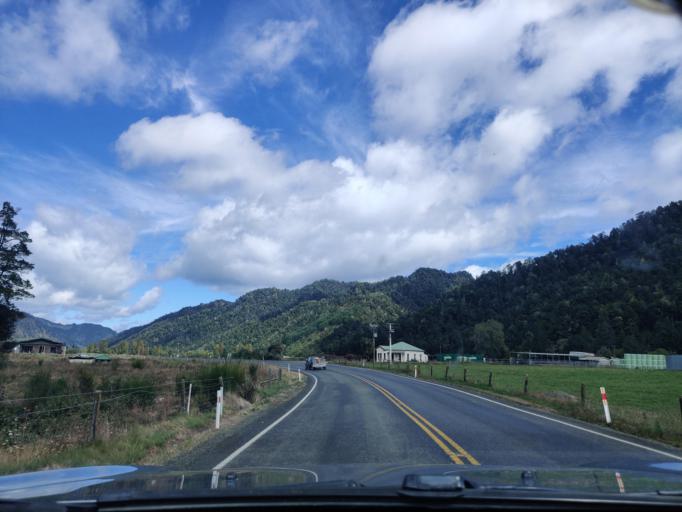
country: NZ
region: Tasman
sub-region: Tasman District
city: Wakefield
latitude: -41.7587
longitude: 172.3883
